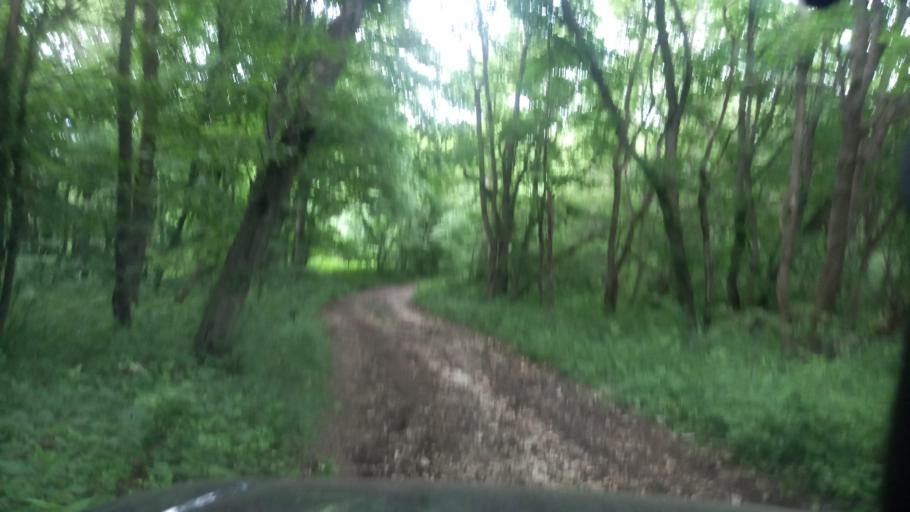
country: RU
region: Karachayevo-Cherkesiya
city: Pregradnaya
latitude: 44.0230
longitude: 41.2946
